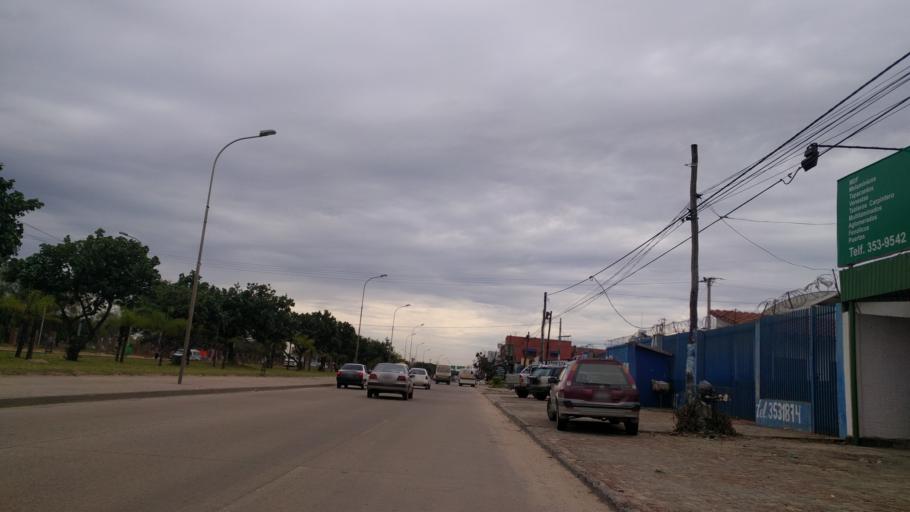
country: BO
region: Santa Cruz
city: Santa Cruz de la Sierra
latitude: -17.8285
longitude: -63.1850
